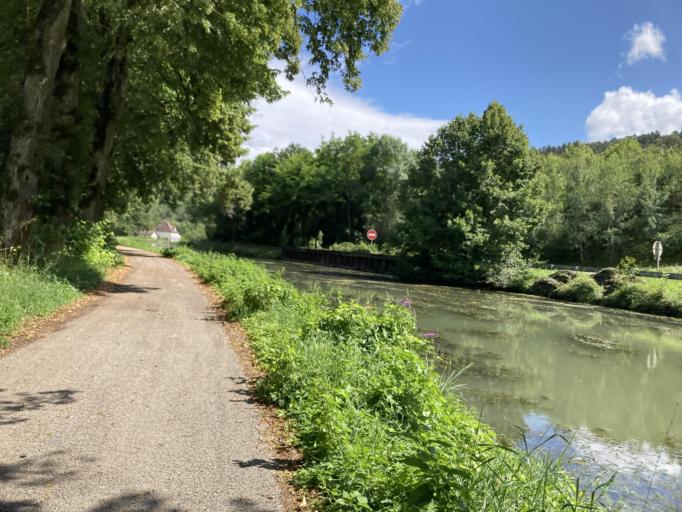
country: FR
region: Bourgogne
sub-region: Departement de la Cote-d'Or
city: Plombieres-les-Dijon
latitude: 47.3314
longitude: 4.9809
